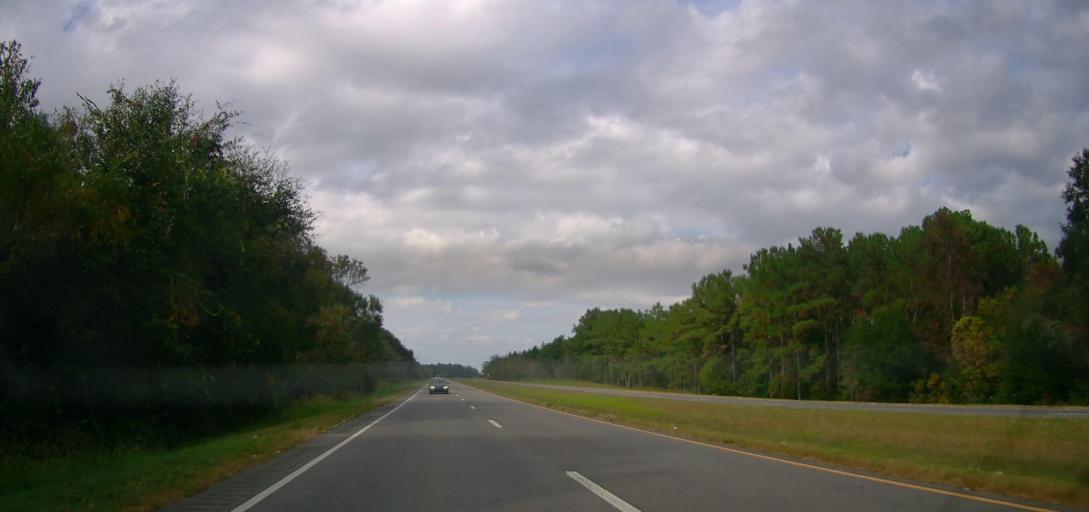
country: US
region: Georgia
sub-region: Thomas County
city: Meigs
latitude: 31.0391
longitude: -84.0668
